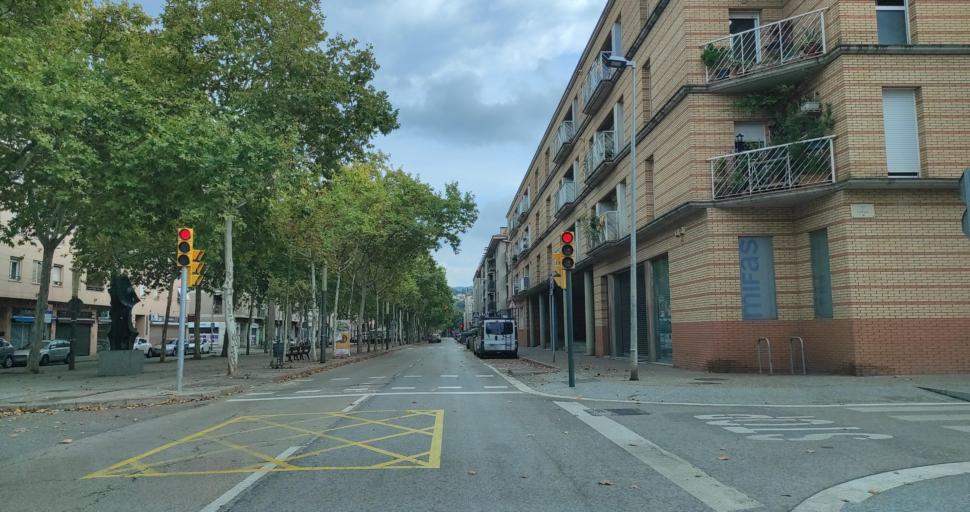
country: ES
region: Catalonia
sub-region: Provincia de Girona
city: Girona
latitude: 41.9922
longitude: 2.8129
